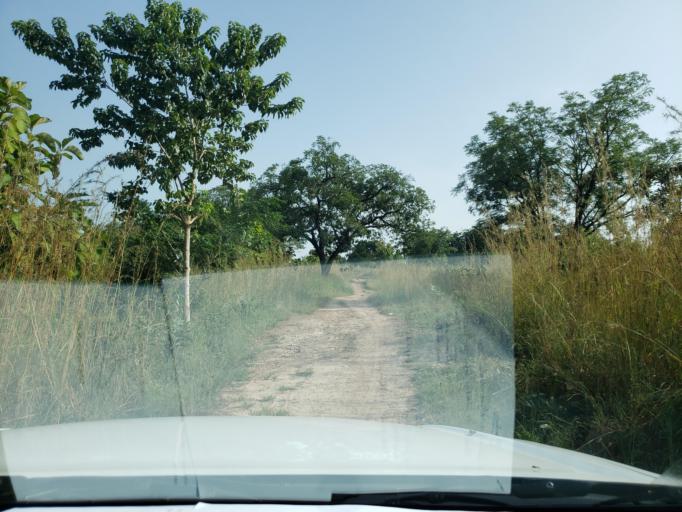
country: TG
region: Kara
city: Bafilo
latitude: 9.4077
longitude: 1.1749
